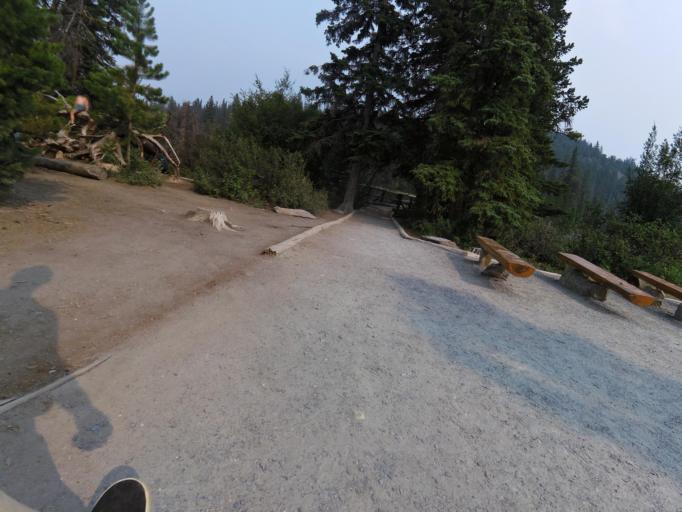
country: CA
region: Alberta
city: Jasper Park Lodge
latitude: 52.9246
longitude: -118.0977
